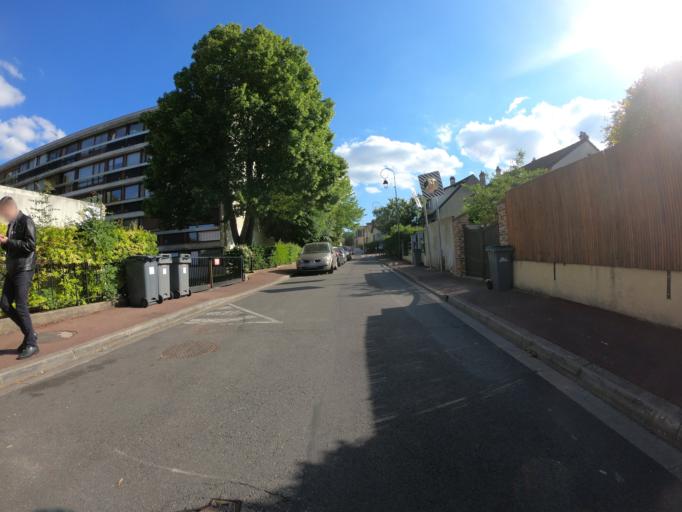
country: FR
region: Ile-de-France
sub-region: Departement des Hauts-de-Seine
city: Antony
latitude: 48.7423
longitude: 2.3049
